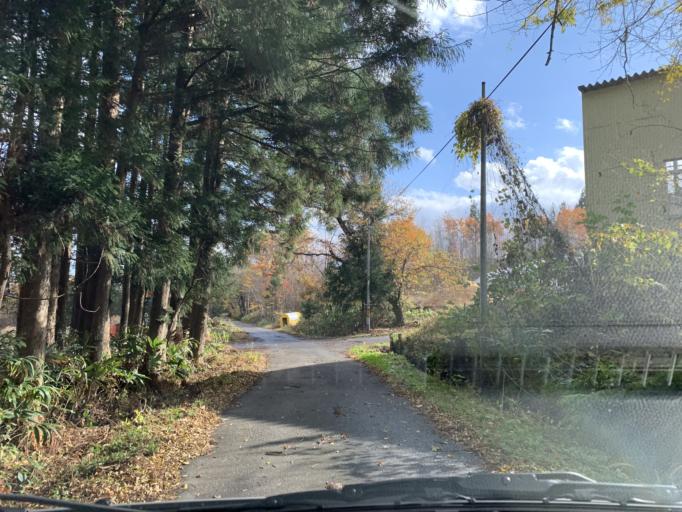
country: JP
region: Iwate
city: Mizusawa
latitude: 39.1026
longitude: 140.9832
